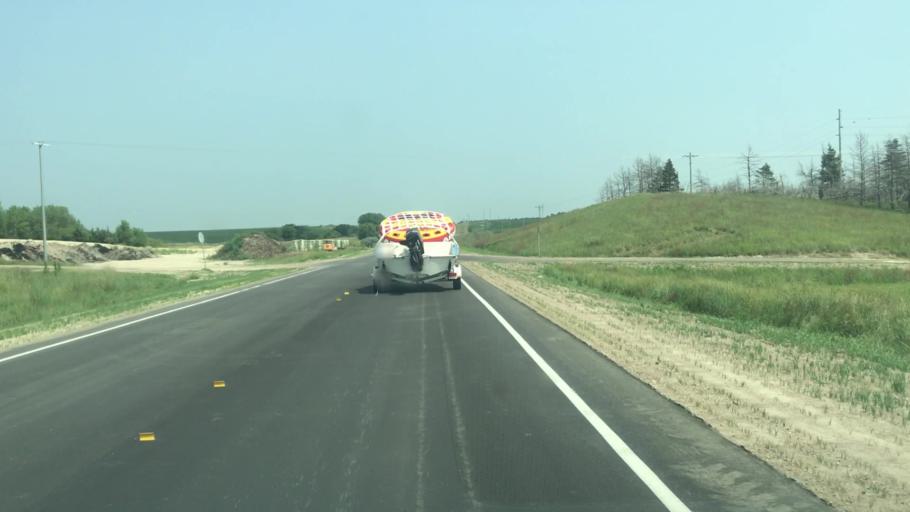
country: US
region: Nebraska
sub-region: Sherman County
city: Loup City
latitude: 41.2637
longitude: -98.9198
